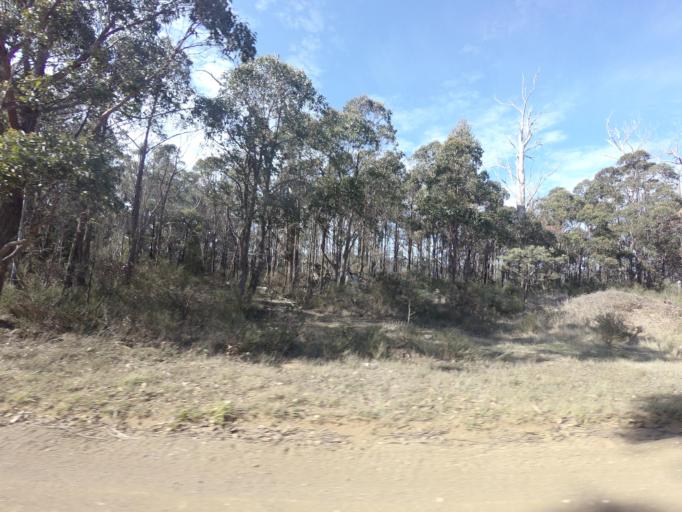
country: AU
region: Tasmania
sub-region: Sorell
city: Sorell
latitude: -42.4763
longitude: 147.4752
